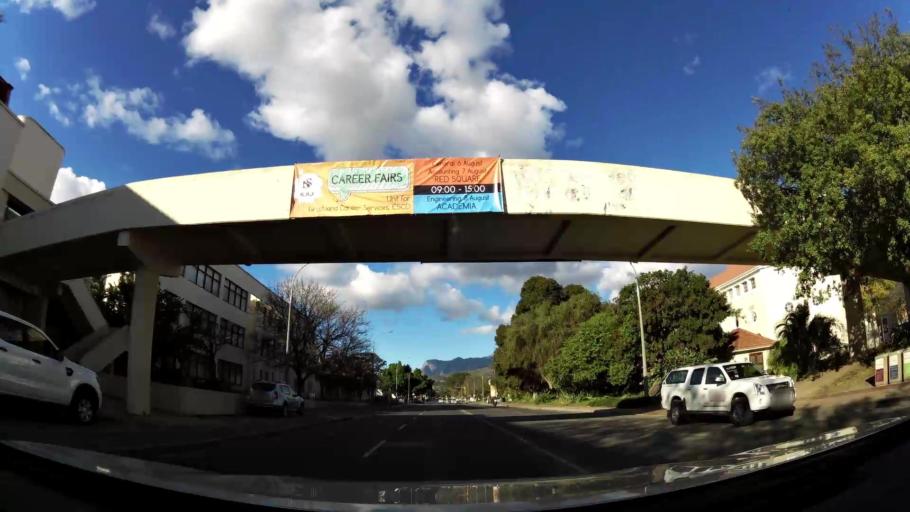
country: ZA
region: Western Cape
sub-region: Cape Winelands District Municipality
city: Stellenbosch
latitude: -33.9314
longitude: 18.8655
